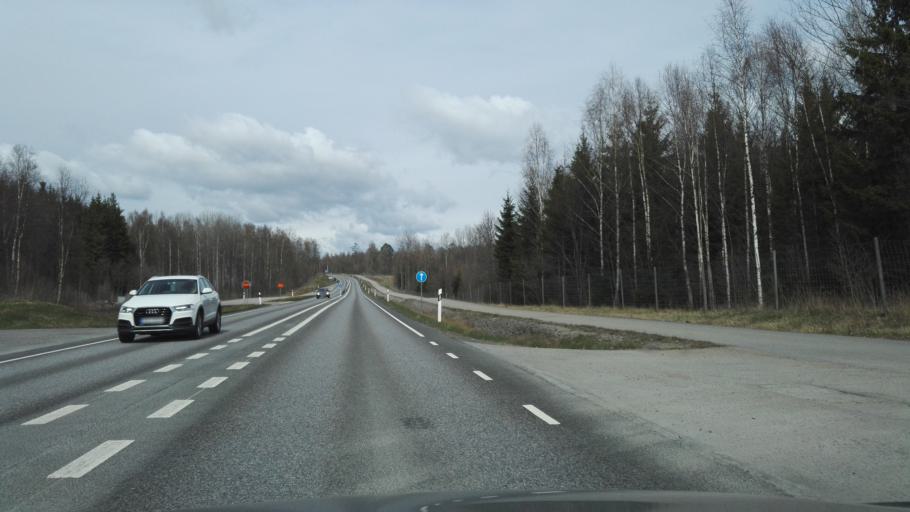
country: SE
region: Kronoberg
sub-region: Vaxjo Kommun
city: Vaexjoe
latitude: 56.9278
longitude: 14.8630
